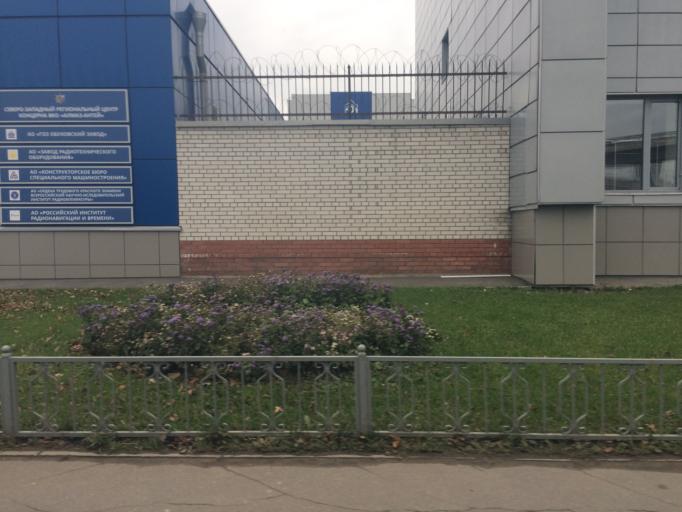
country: RU
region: Leningrad
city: Rybatskoye
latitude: 59.8547
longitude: 30.4808
